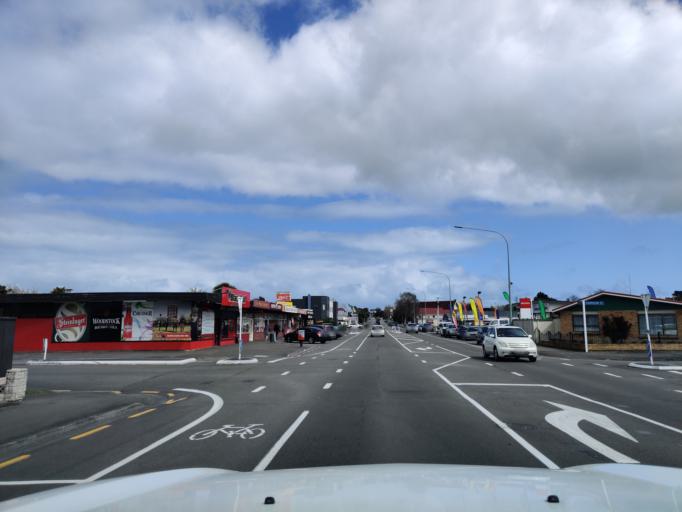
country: NZ
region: Manawatu-Wanganui
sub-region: Wanganui District
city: Wanganui
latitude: -39.9243
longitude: 175.0472
